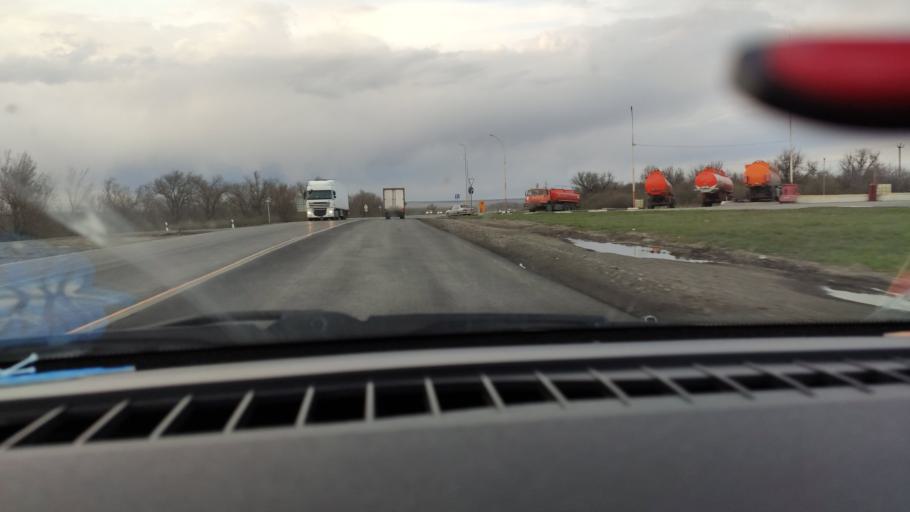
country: RU
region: Saratov
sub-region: Saratovskiy Rayon
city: Saratov
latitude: 51.6860
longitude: 46.0035
